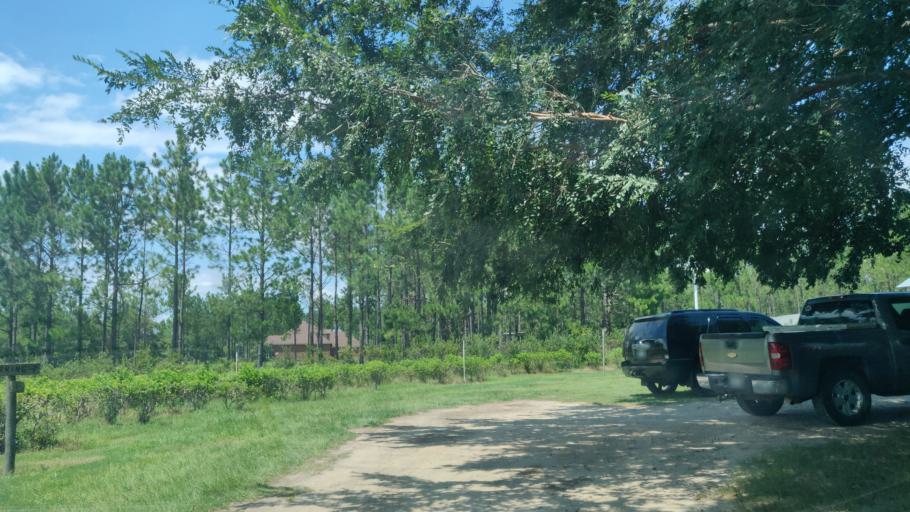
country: US
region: Georgia
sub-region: Tift County
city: Omega
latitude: 31.4293
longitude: -83.6358
